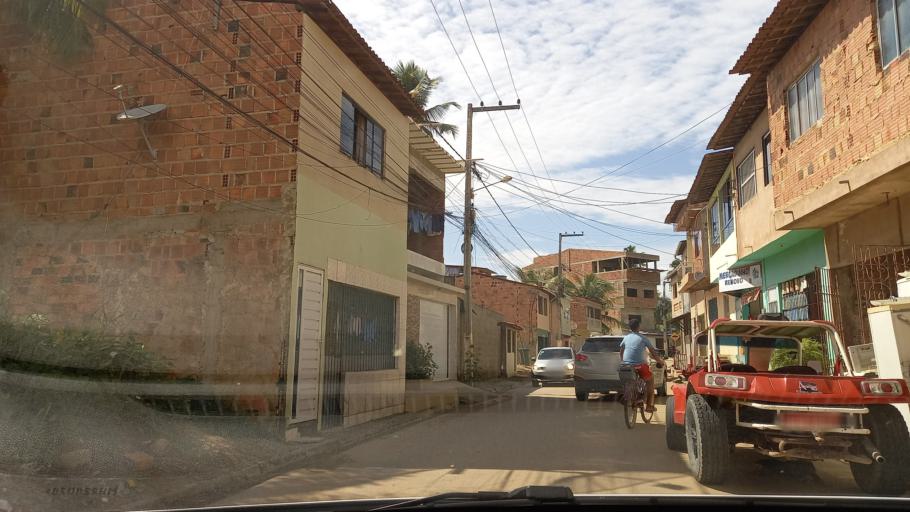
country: BR
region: Alagoas
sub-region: Maragogi
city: Maragogi
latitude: -9.0046
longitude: -35.2189
